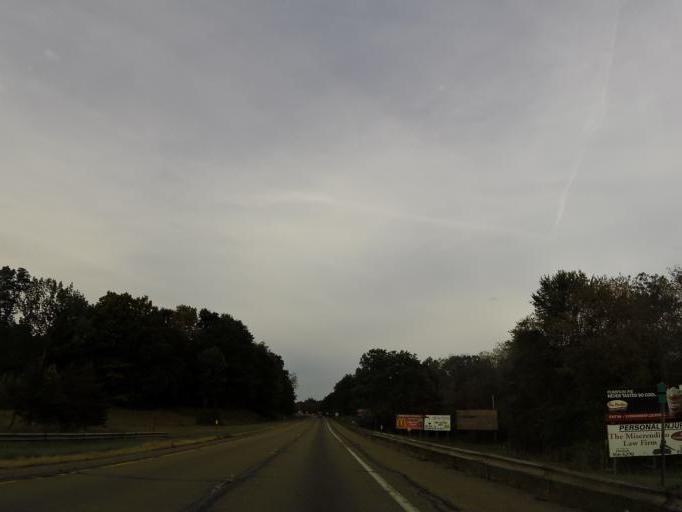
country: US
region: New York
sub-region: Erie County
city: Lake Erie Beach
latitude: 42.5792
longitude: -79.0706
